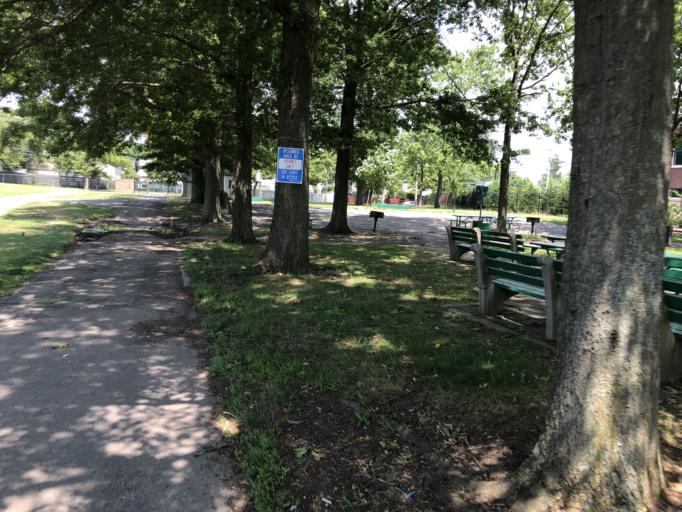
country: US
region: New York
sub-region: Nassau County
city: Hewlett
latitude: 40.6458
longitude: -73.6903
